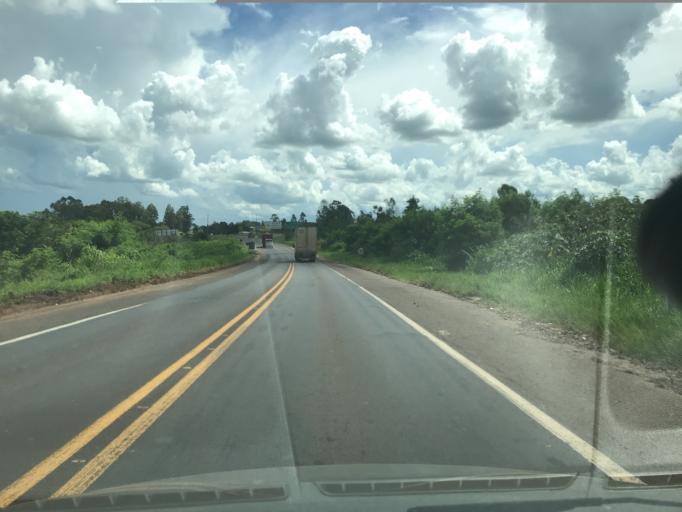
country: BR
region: Parana
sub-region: Cruzeiro Do Oeste
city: Cruzeiro do Oeste
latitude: -23.7932
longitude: -53.0439
